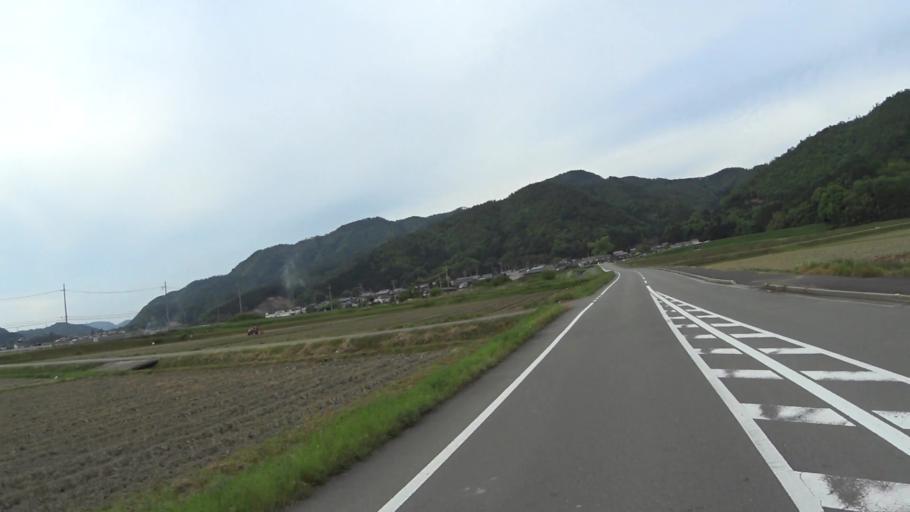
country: JP
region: Kyoto
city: Kameoka
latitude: 35.0919
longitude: 135.5478
